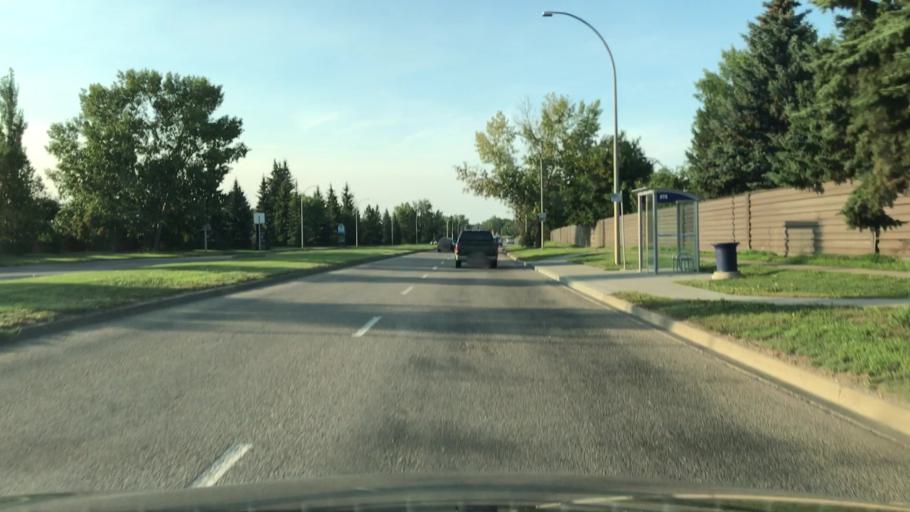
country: CA
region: Alberta
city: Beaumont
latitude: 53.4462
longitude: -113.4193
